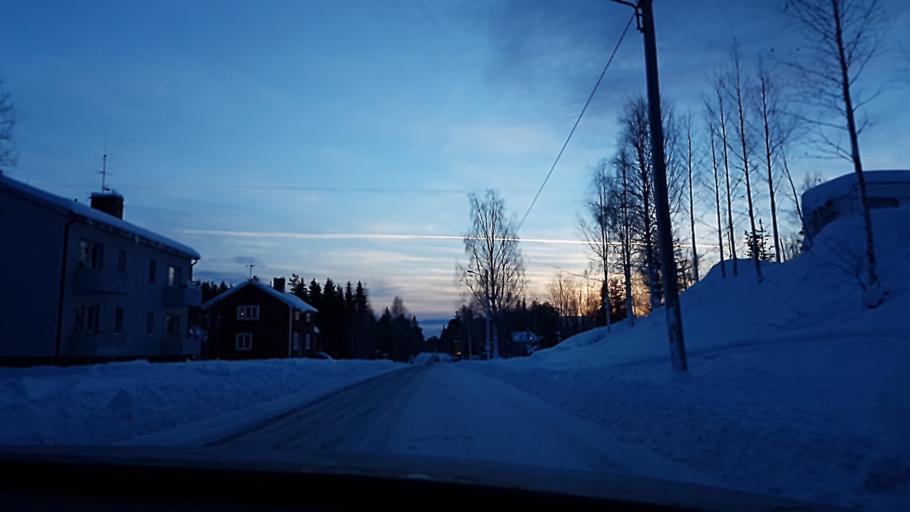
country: SE
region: Norrbotten
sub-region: Jokkmokks Kommun
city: Jokkmokk
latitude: 66.1475
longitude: 19.9886
